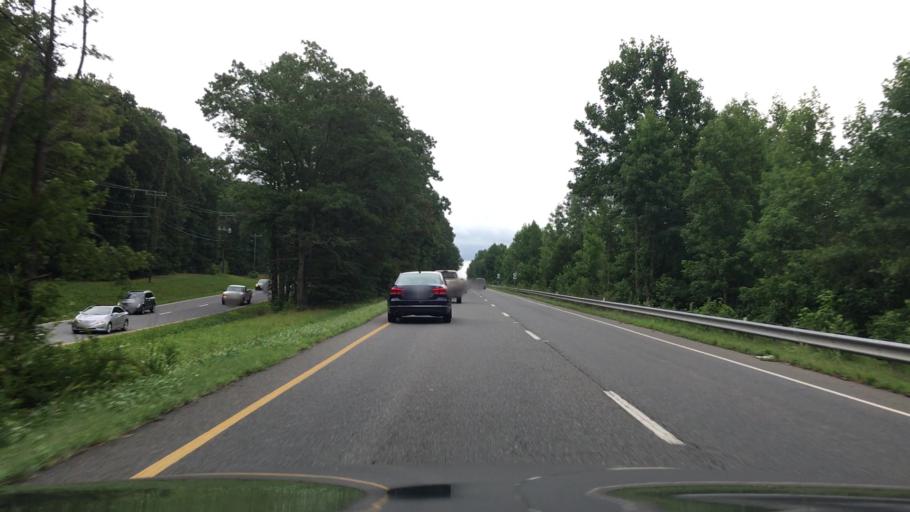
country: US
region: Virginia
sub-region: Spotsylvania County
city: Spotsylvania
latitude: 38.3037
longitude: -77.6211
